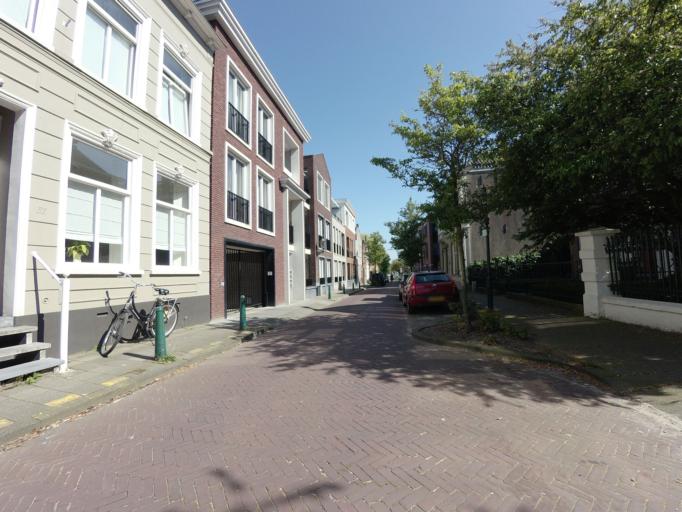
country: NL
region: North Brabant
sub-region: Gemeente Moerdijk
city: Klundert
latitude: 51.6438
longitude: 4.6088
